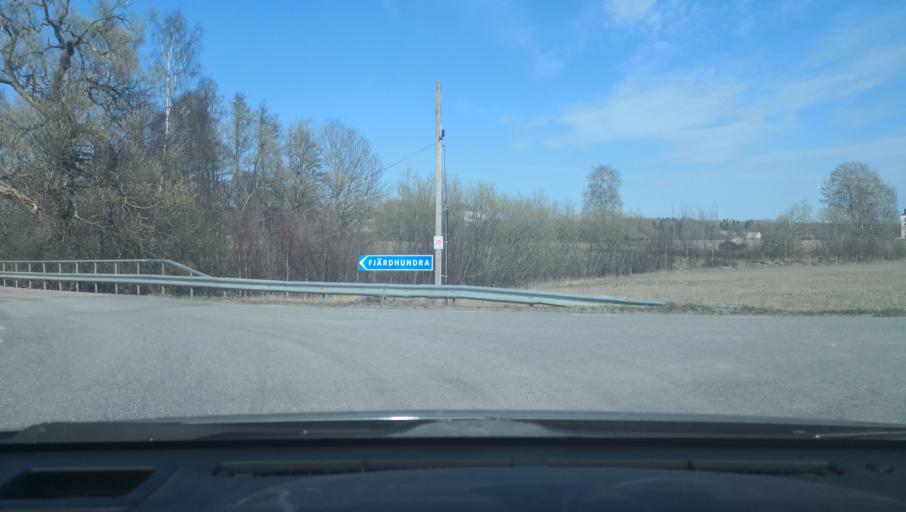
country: SE
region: Uppsala
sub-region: Enkopings Kommun
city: Irsta
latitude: 59.7720
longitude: 16.8837
